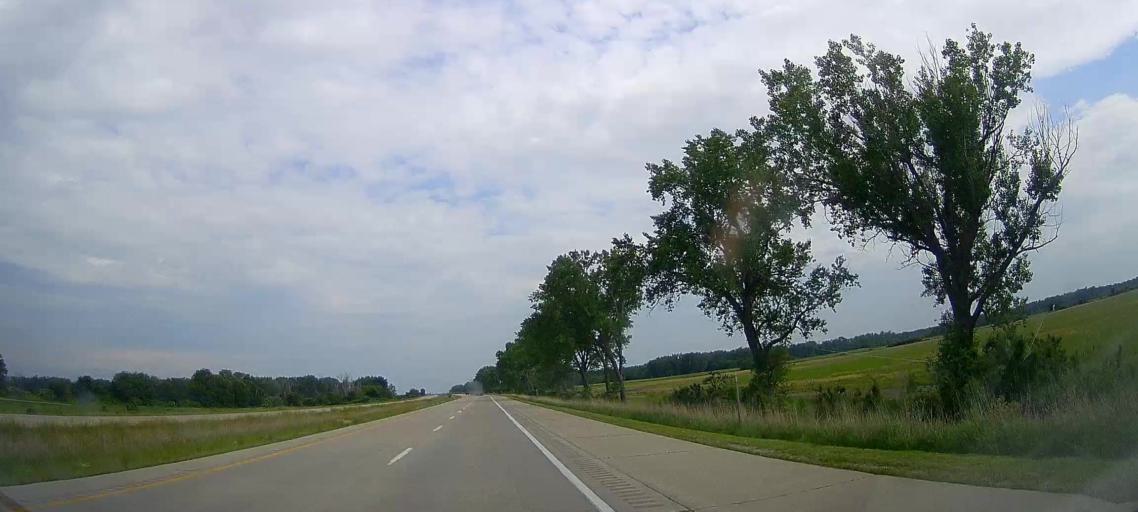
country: US
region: Nebraska
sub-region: Burt County
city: Tekamah
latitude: 41.8257
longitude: -96.0770
